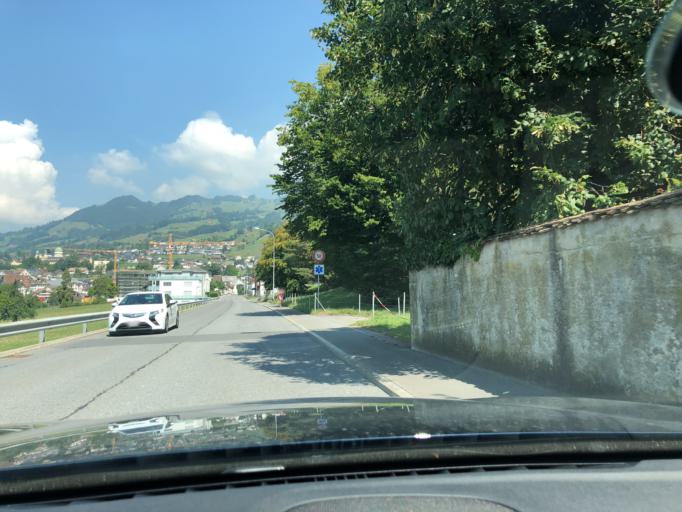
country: CH
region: Schwyz
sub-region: Bezirk Schwyz
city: Schwyz
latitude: 47.0149
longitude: 8.6579
